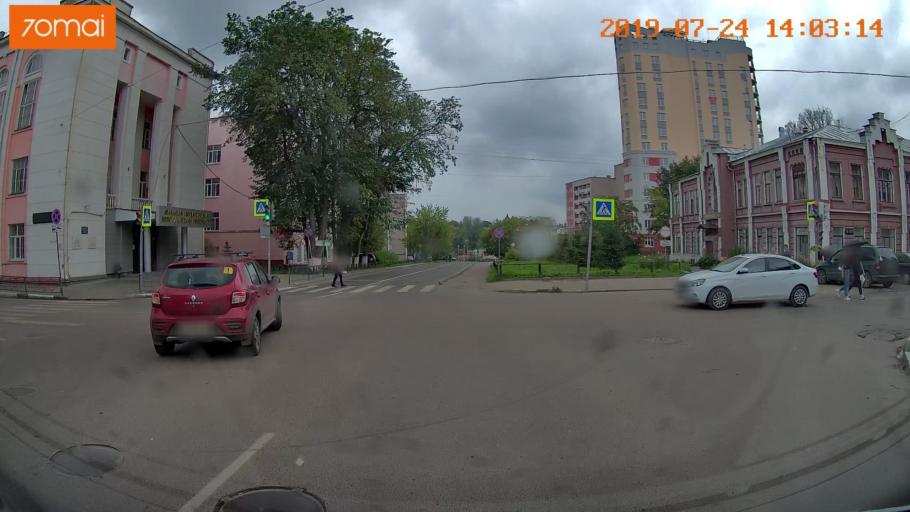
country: RU
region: Ivanovo
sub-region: Gorod Ivanovo
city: Ivanovo
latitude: 57.0060
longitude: 40.9802
